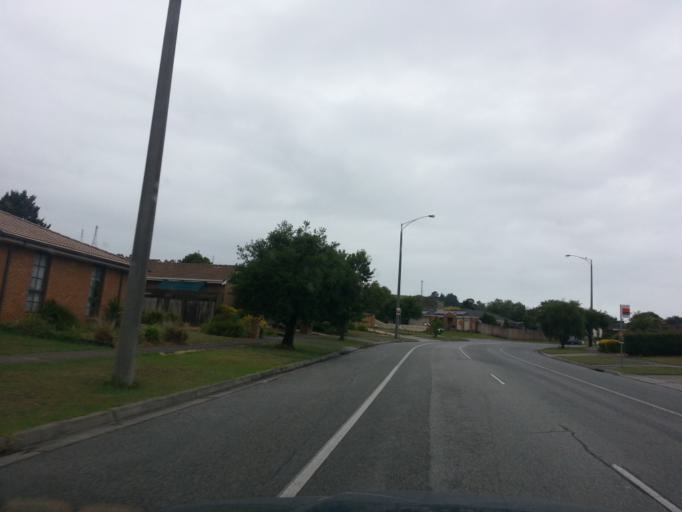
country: AU
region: Victoria
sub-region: Casey
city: Narre Warren North
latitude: -38.0024
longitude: 145.3160
